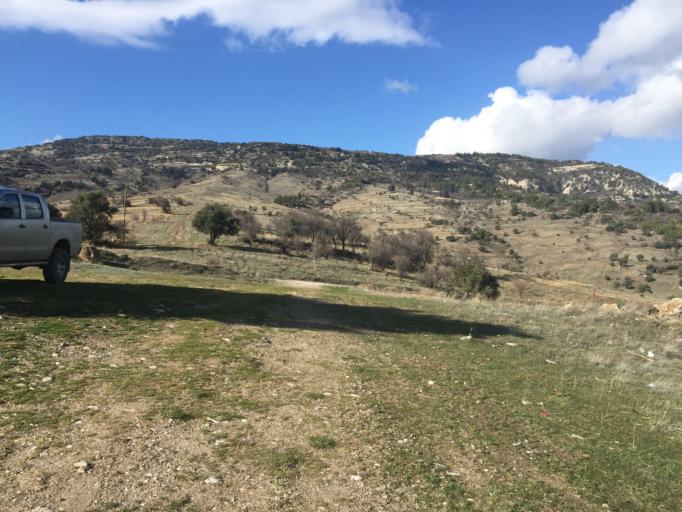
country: CY
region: Limassol
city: Pachna
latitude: 34.8861
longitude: 32.6528
